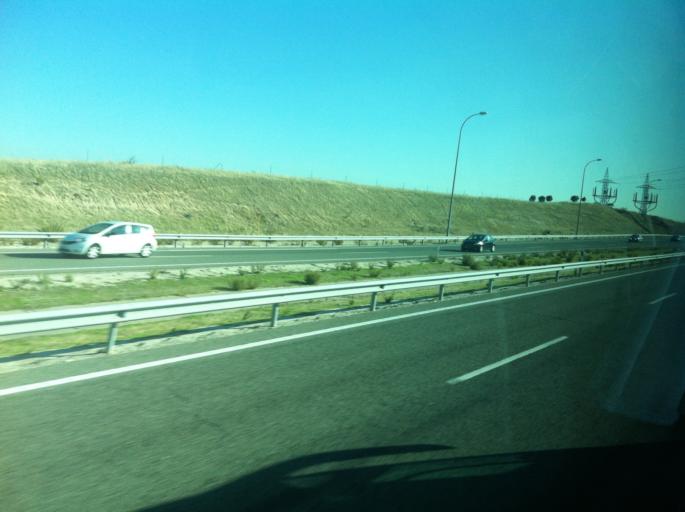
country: ES
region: Madrid
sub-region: Provincia de Madrid
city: San Sebastian de los Reyes
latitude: 40.5124
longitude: -3.5987
